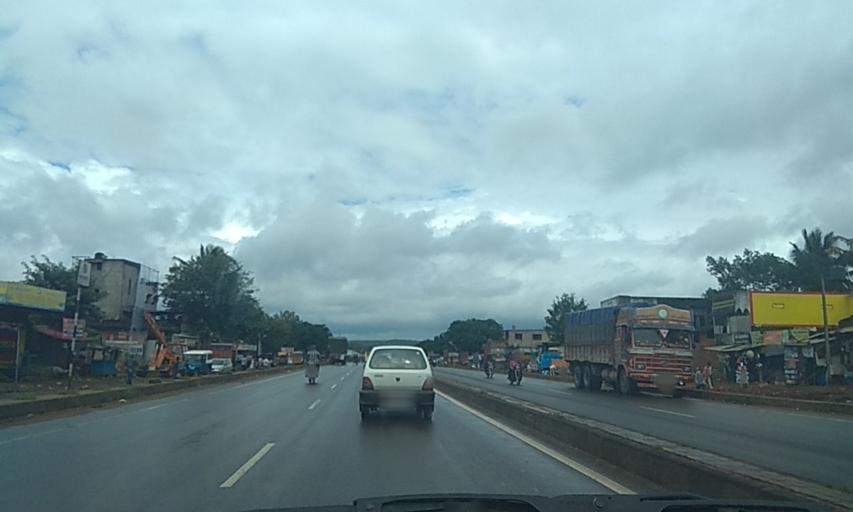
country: IN
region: Karnataka
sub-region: Belgaum
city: Belgaum
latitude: 15.9381
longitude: 74.5256
